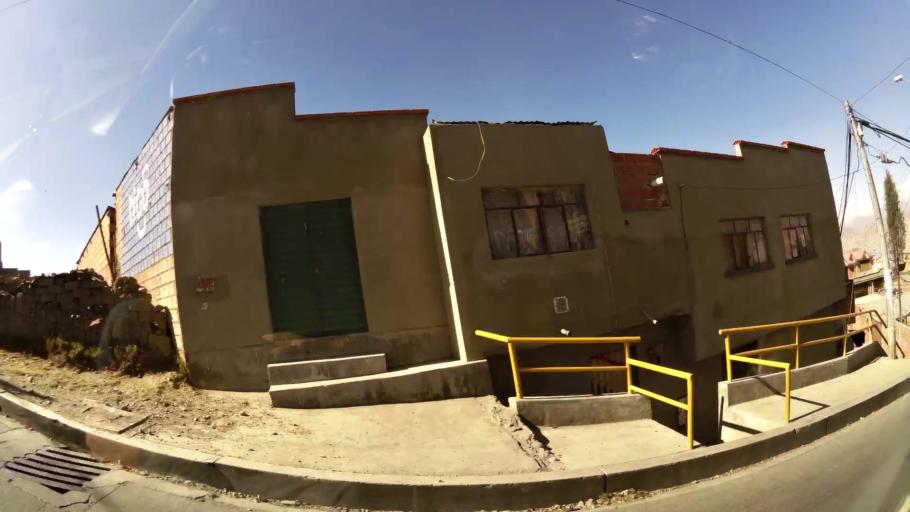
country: BO
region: La Paz
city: La Paz
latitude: -16.5220
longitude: -68.1445
